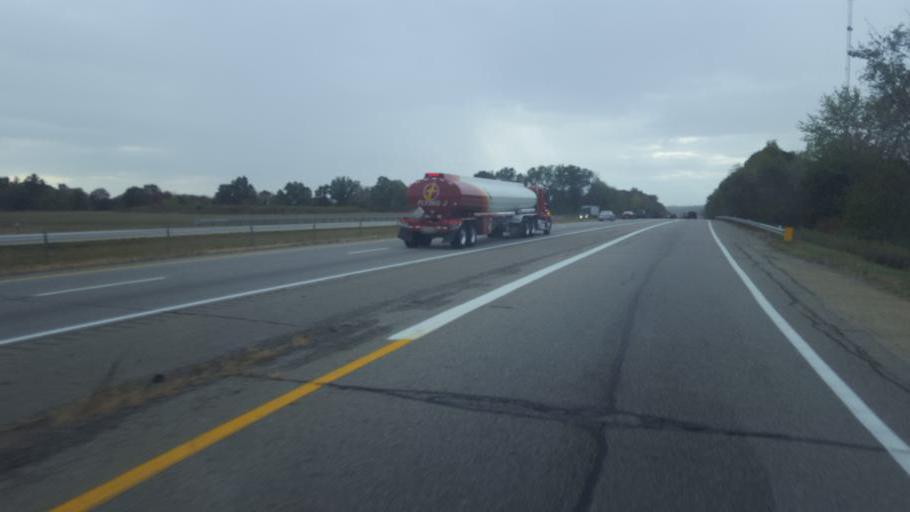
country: US
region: Ohio
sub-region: Portage County
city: Brimfield
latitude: 41.1074
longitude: -81.3512
